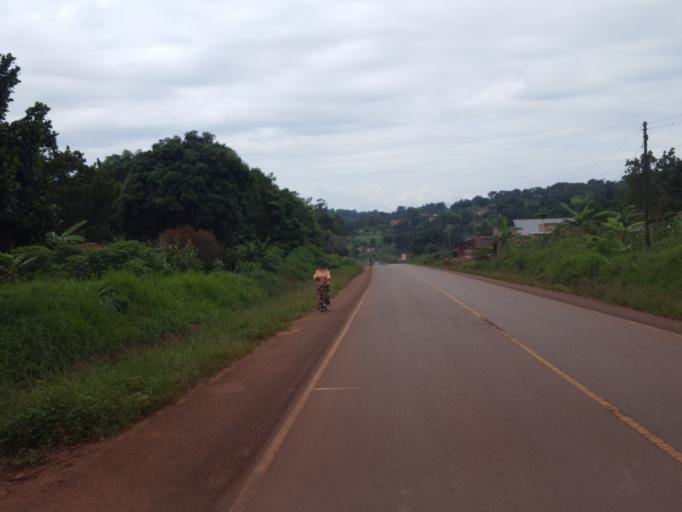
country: UG
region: Central Region
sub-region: Mityana District
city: Mityana
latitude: 0.6592
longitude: 32.0919
